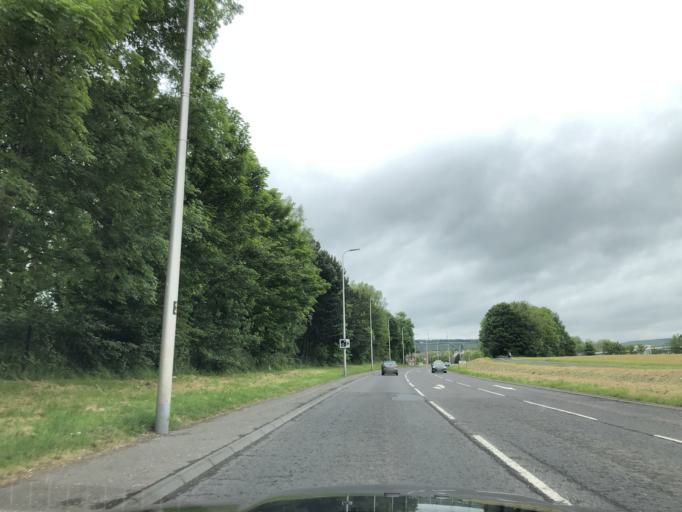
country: GB
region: Northern Ireland
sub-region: Lisburn District
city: Lisburn
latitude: 54.5199
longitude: -6.0722
